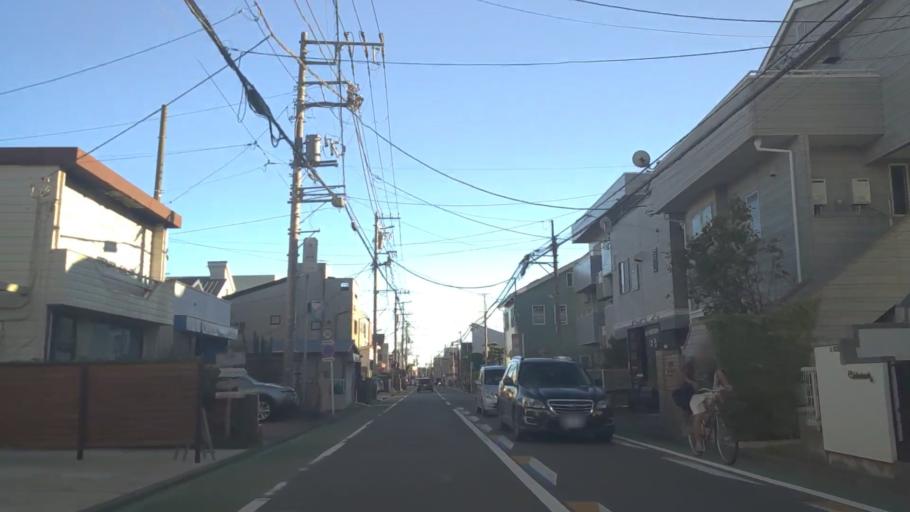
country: JP
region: Kanagawa
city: Chigasaki
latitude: 35.3274
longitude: 139.4146
